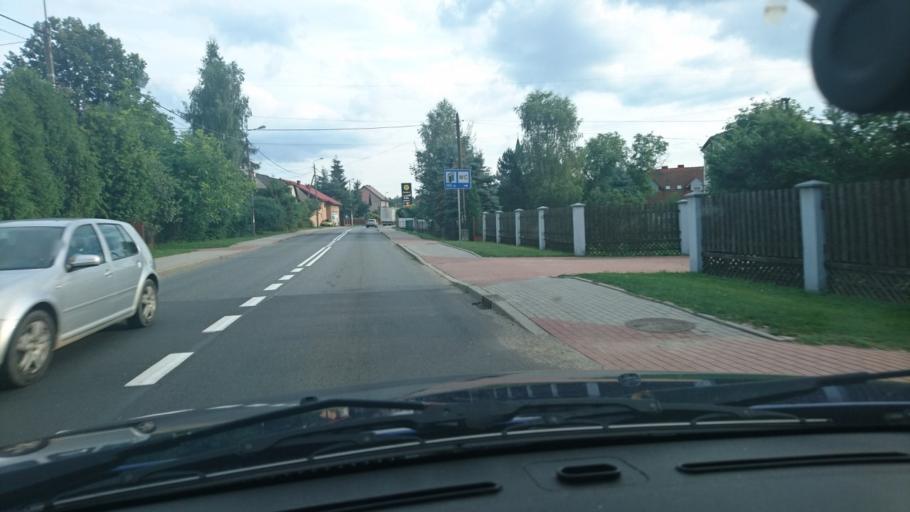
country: PL
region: Silesian Voivodeship
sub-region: Powiat zywiecki
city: Cisiec
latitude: 49.5871
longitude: 19.1032
